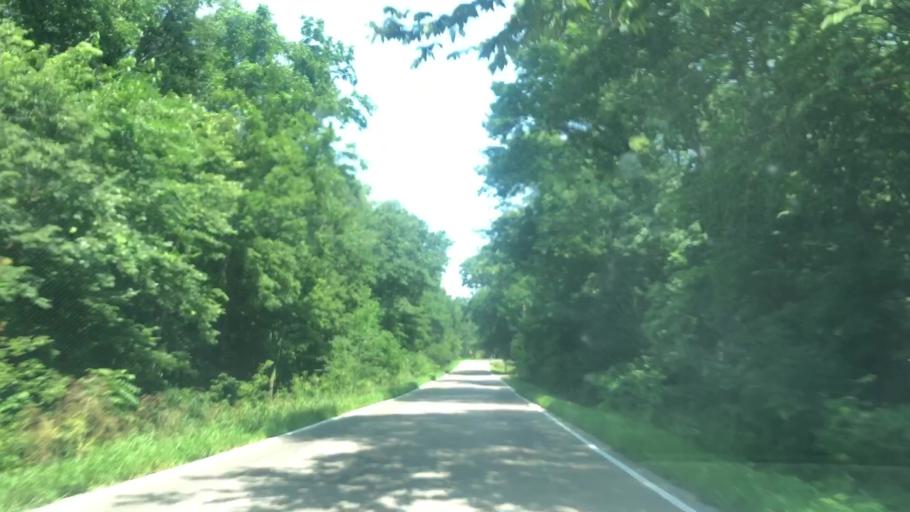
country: US
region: Iowa
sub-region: Marshall County
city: Marshalltown
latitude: 42.0265
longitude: -92.9459
